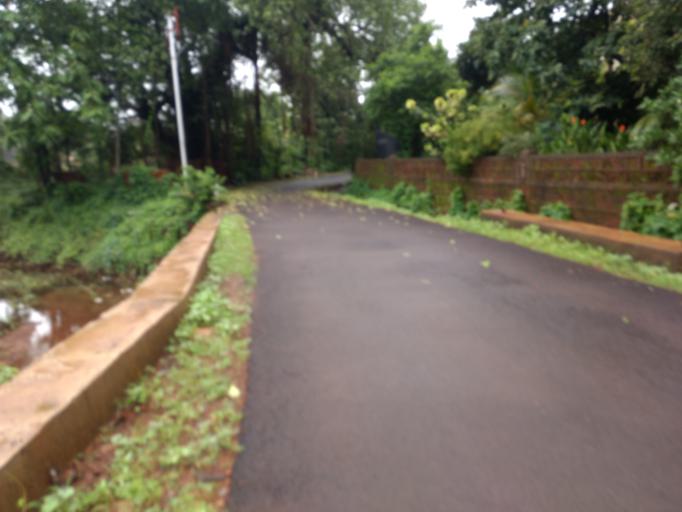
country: IN
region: Maharashtra
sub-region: Ratnagiri
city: Guhagar
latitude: 17.4941
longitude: 73.1894
